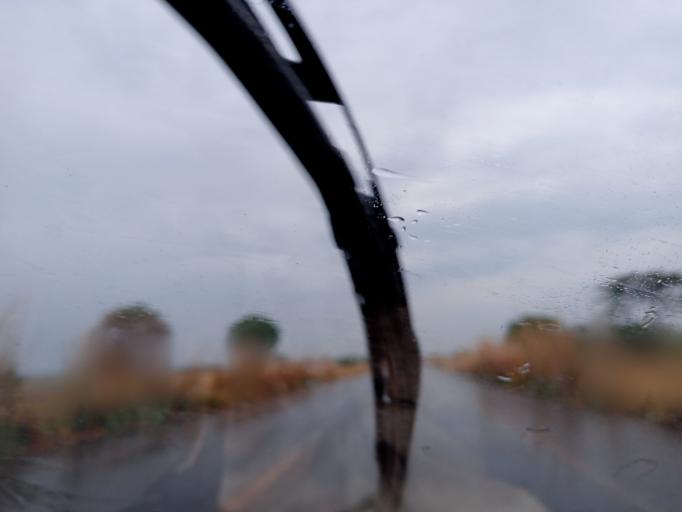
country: BR
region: Minas Gerais
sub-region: Ituiutaba
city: Ituiutaba
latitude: -19.0912
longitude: -49.5106
